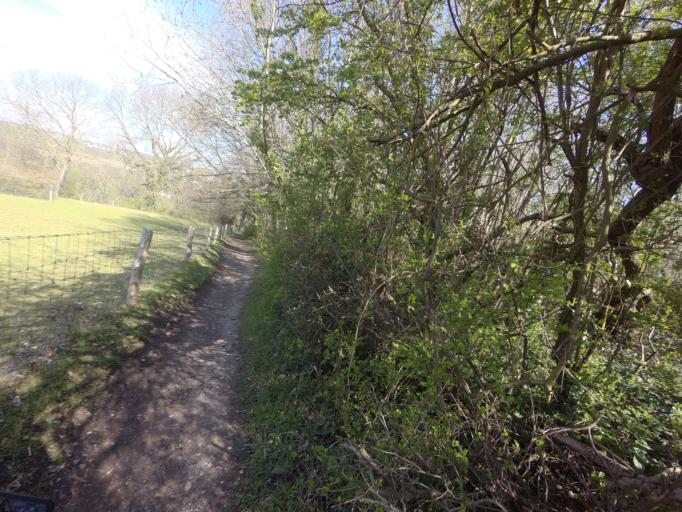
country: NL
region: Limburg
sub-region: Gemeente Maastricht
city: Maastricht
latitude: 50.8266
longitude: 5.6778
